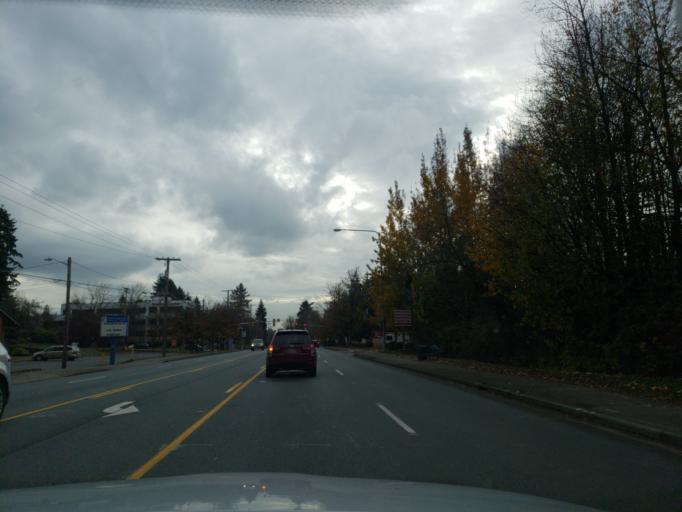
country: US
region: Washington
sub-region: King County
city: Woodinville
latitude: 47.7528
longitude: -122.1528
